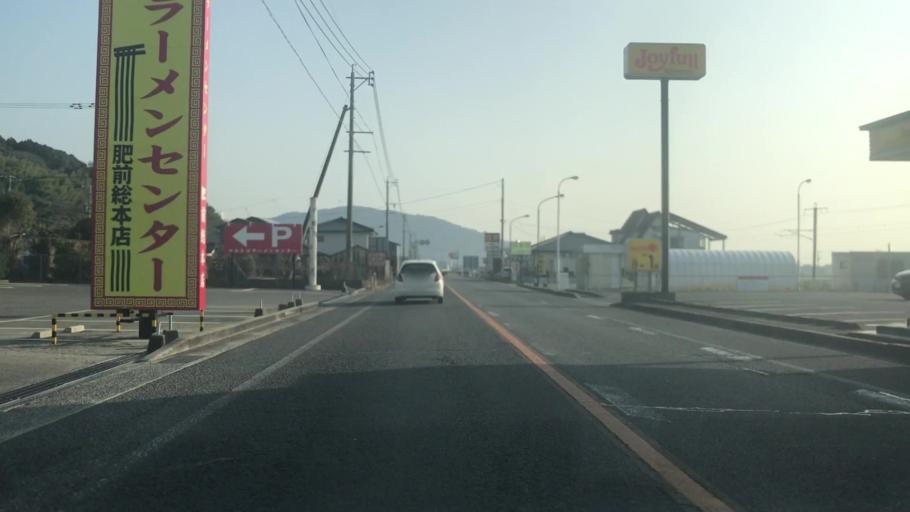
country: JP
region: Saga Prefecture
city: Takeocho-takeo
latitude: 33.2146
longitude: 130.1279
